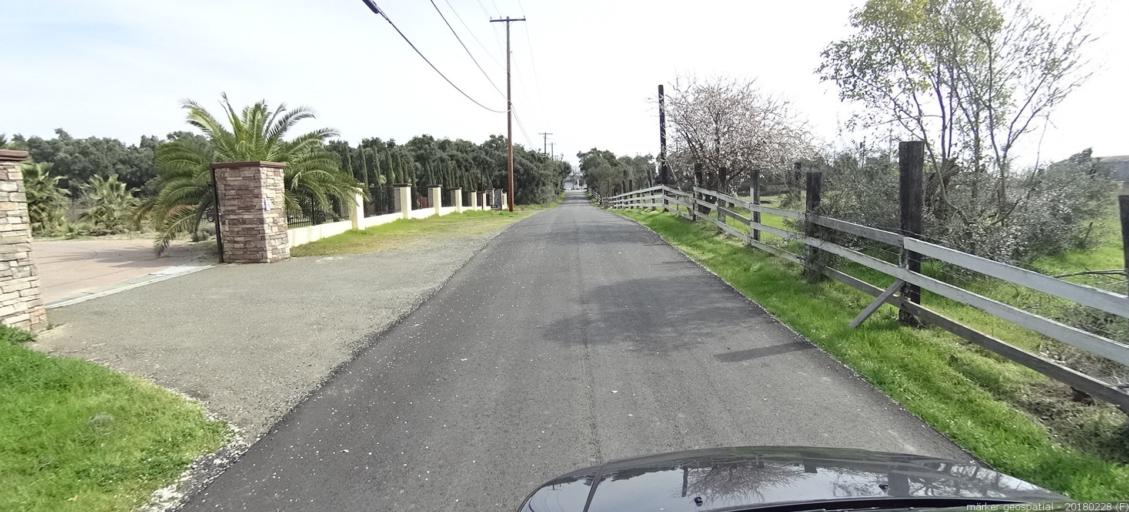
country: US
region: California
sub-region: Sacramento County
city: Antelope
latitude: 38.7172
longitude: -121.3298
